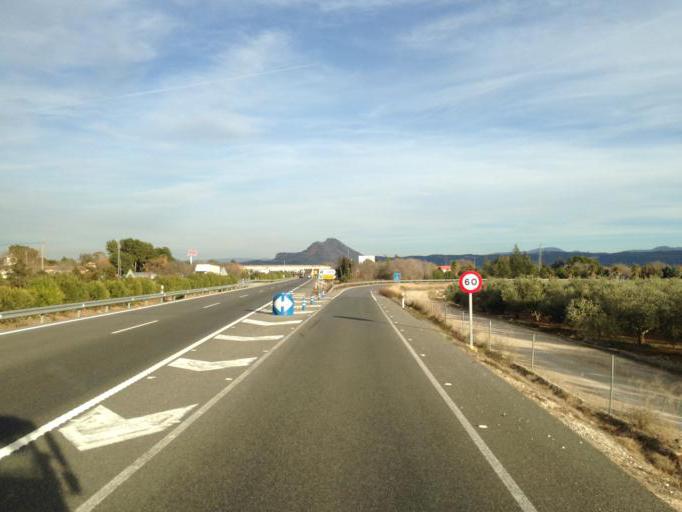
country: ES
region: Andalusia
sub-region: Provincia de Malaga
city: Antequera
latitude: 37.0719
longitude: -4.5704
